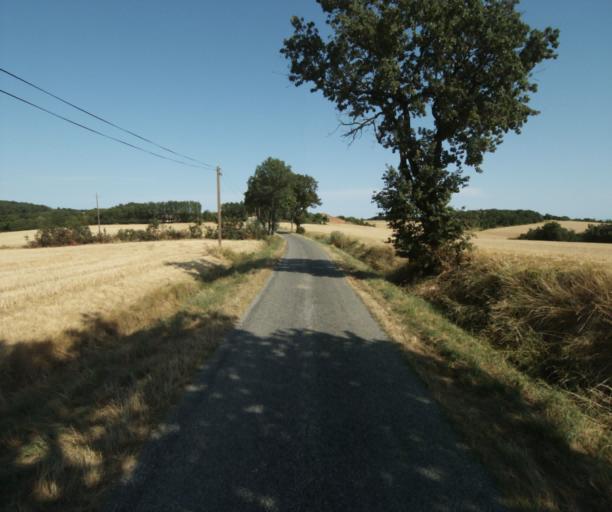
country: FR
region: Midi-Pyrenees
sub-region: Departement de la Haute-Garonne
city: Saint-Felix-Lauragais
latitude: 43.4268
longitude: 1.8289
